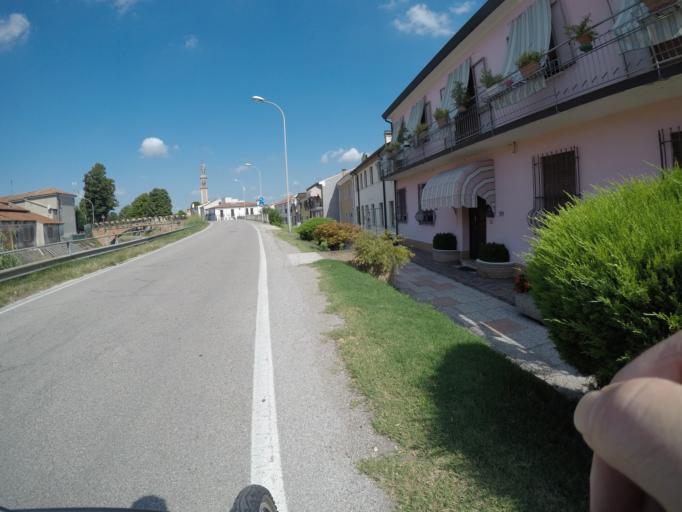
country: IT
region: Veneto
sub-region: Provincia di Rovigo
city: Lendinara
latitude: 45.0810
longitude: 11.6060
